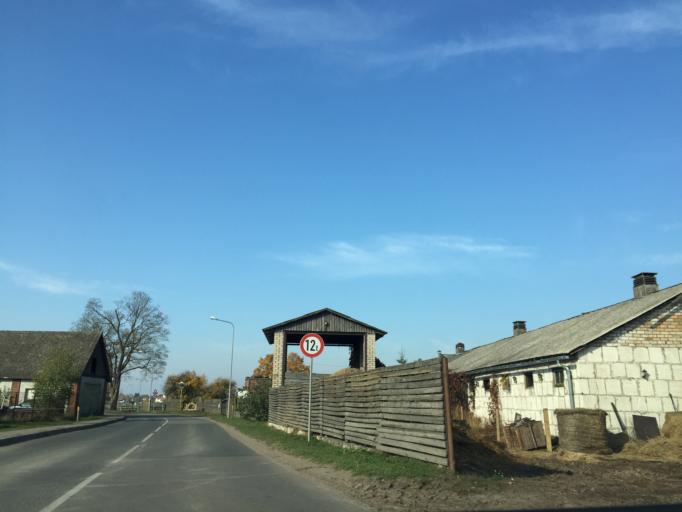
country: LV
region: Marupe
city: Marupe
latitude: 56.8878
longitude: 24.0658
